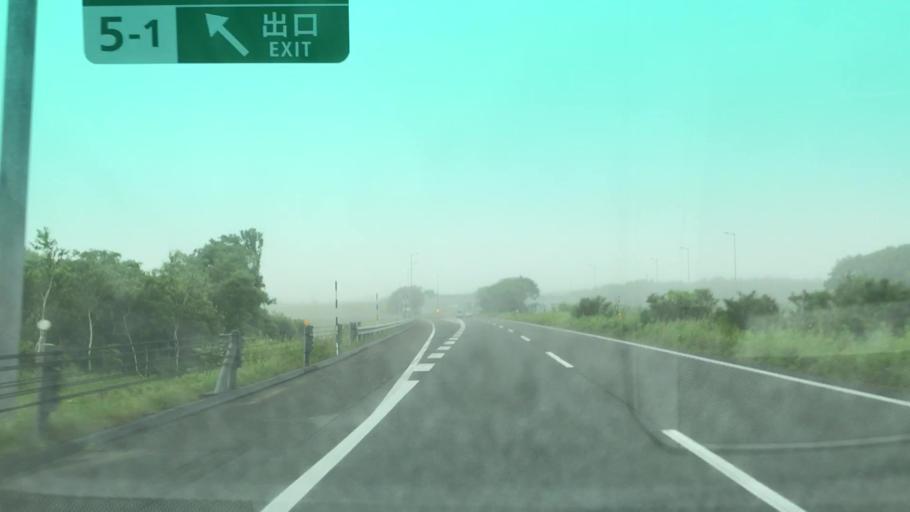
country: JP
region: Hokkaido
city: Chitose
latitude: 42.7798
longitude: 141.6272
